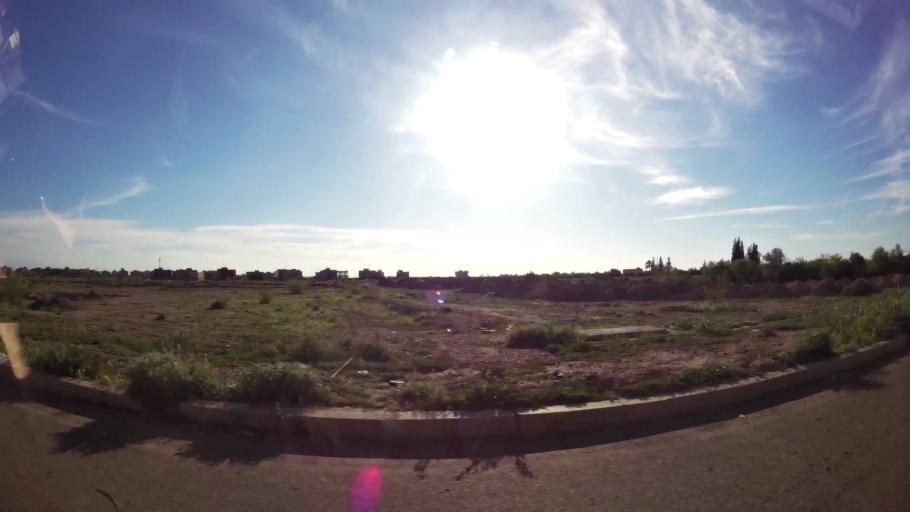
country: MA
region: Marrakech-Tensift-Al Haouz
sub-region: Marrakech
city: Marrakesh
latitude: 31.6779
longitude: -8.0681
